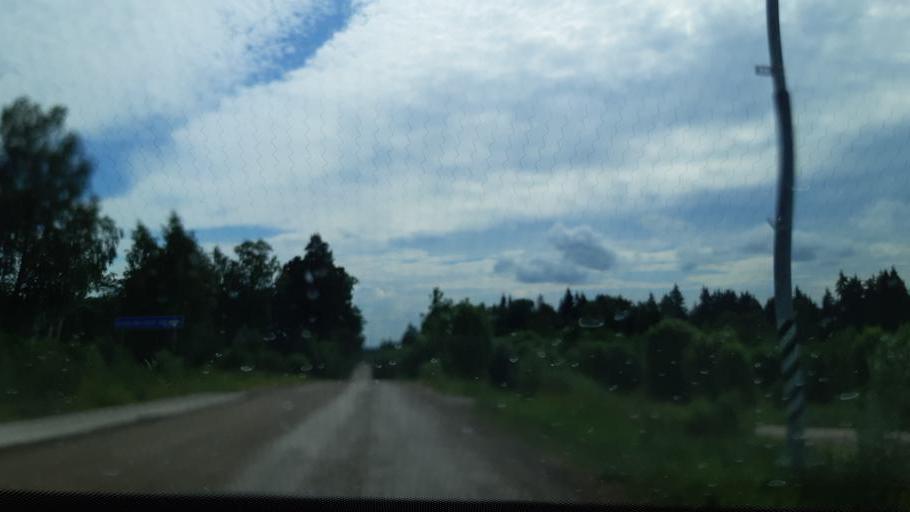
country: RU
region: Moskovskaya
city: Vereya
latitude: 55.2309
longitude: 36.0117
